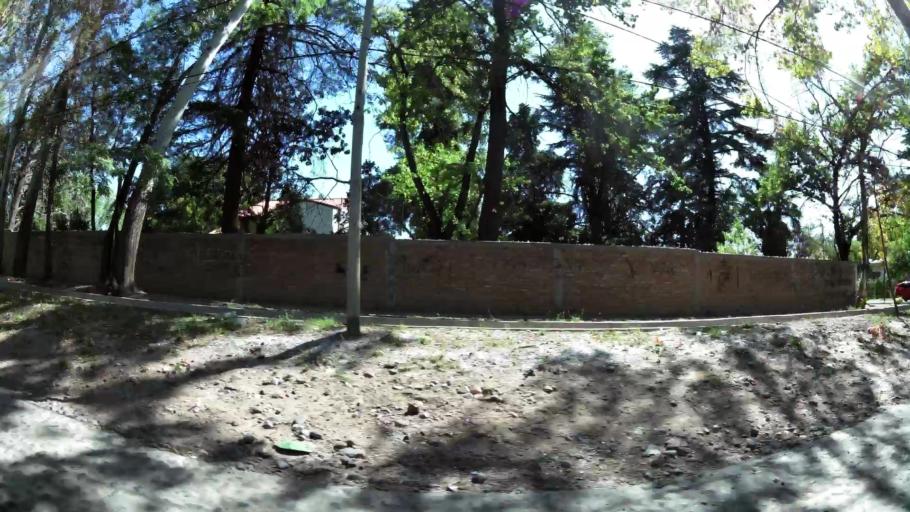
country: AR
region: Mendoza
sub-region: Departamento de Godoy Cruz
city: Godoy Cruz
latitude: -32.9459
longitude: -68.8065
